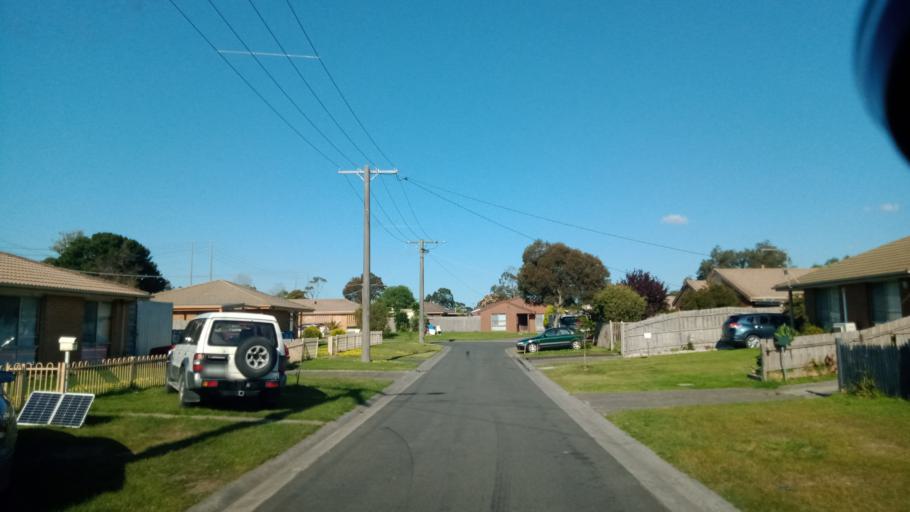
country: AU
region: Victoria
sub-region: Casey
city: Cranbourne North
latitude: -38.0902
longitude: 145.2743
